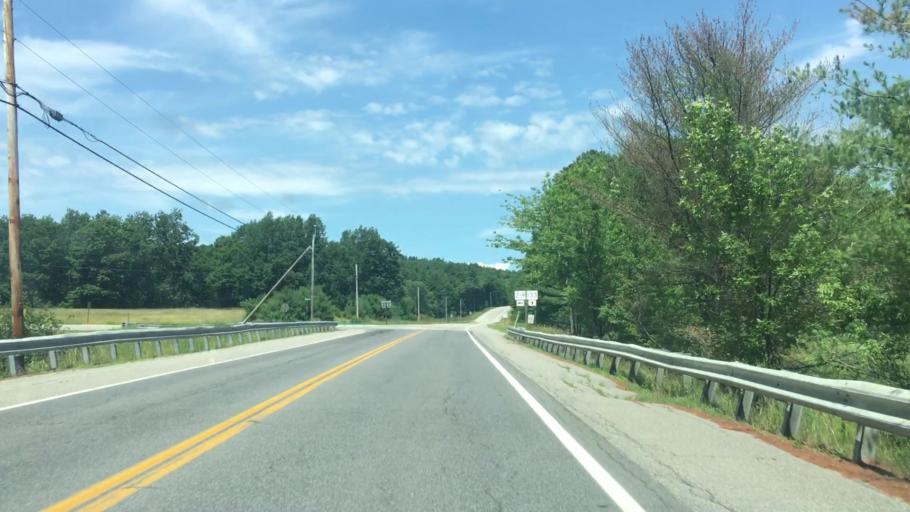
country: US
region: Maine
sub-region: Kennebec County
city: Wayne
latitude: 44.3573
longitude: -70.0811
